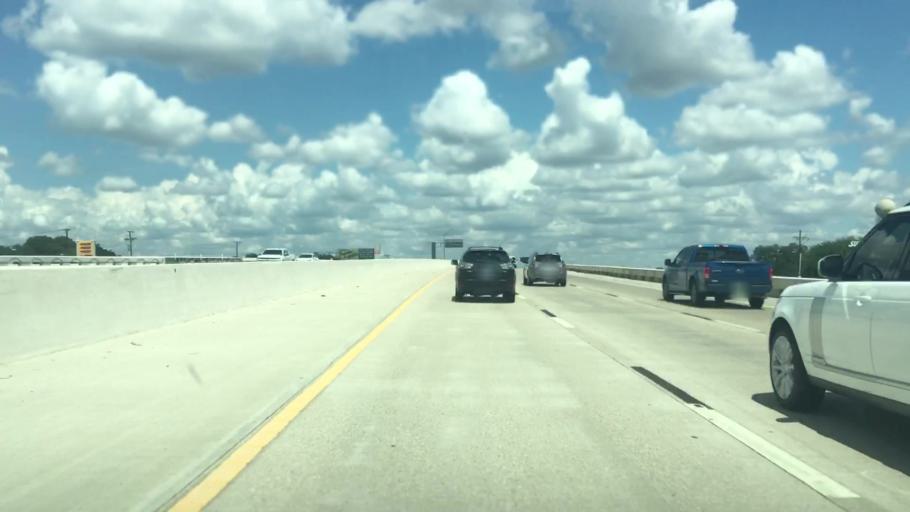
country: US
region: Texas
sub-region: Bell County
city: Salado
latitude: 30.9529
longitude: -97.5371
